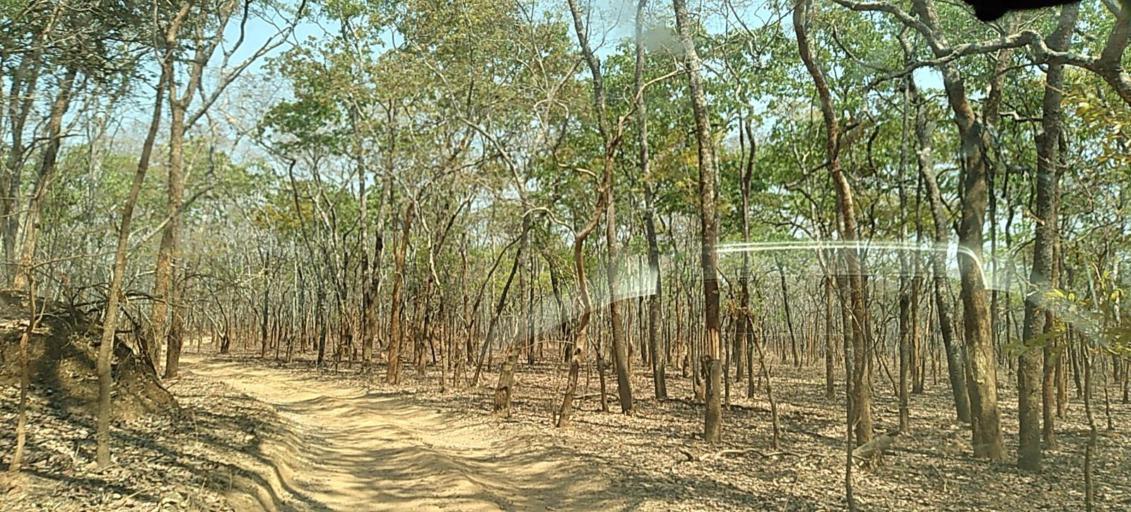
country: ZM
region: North-Western
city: Kasempa
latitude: -13.3933
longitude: 25.6014
